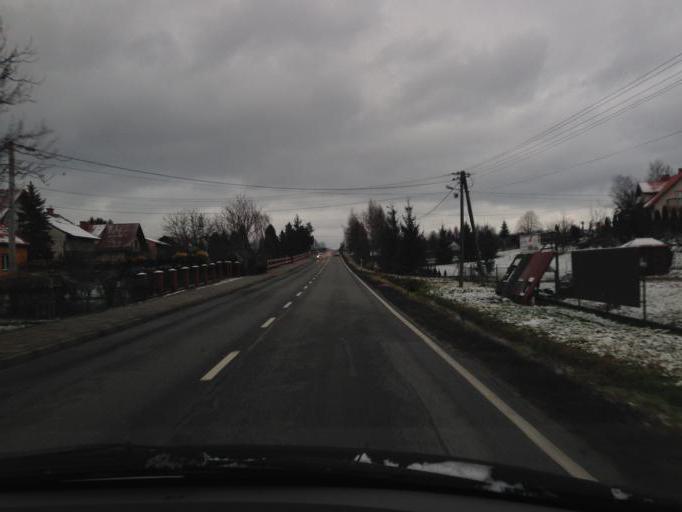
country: PL
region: Lesser Poland Voivodeship
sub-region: Powiat tarnowski
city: Zakliczyn
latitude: 49.8541
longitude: 20.8226
